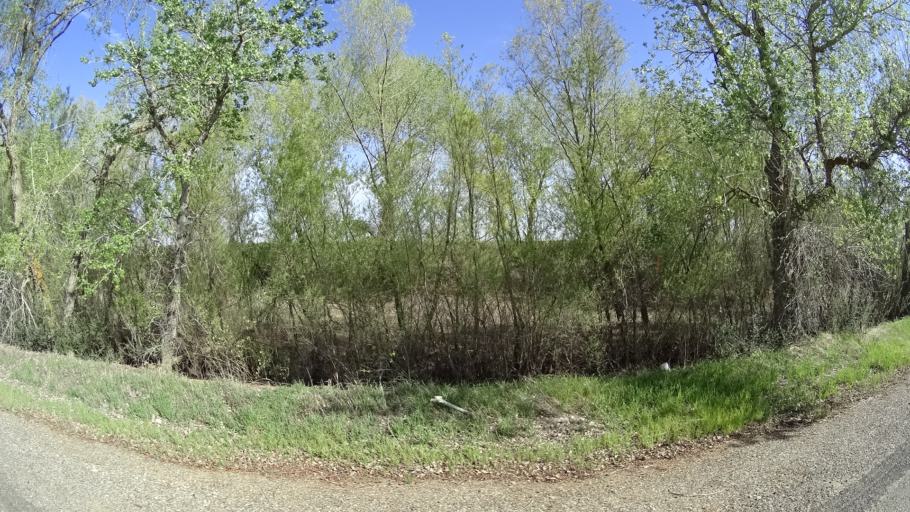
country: US
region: California
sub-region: Glenn County
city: Willows
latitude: 39.6114
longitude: -122.2328
